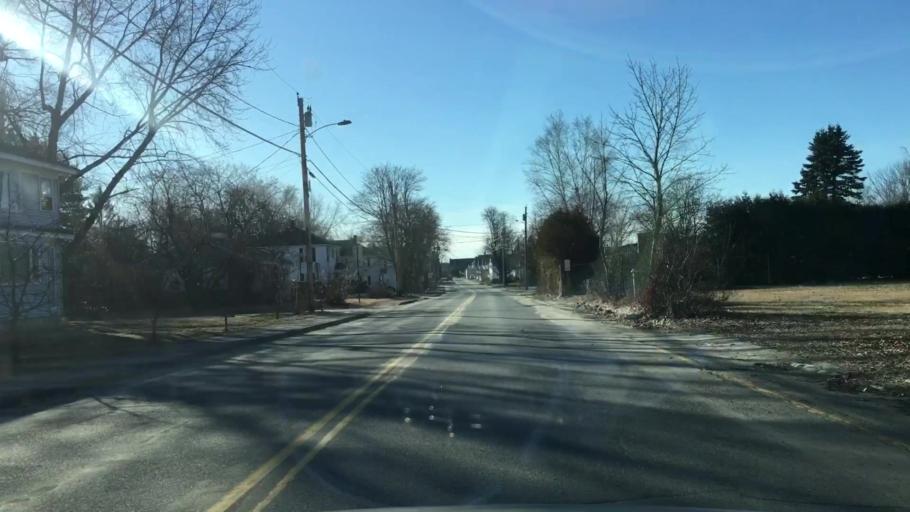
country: US
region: Maine
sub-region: Kennebec County
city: Winslow
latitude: 44.5501
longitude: -69.6209
